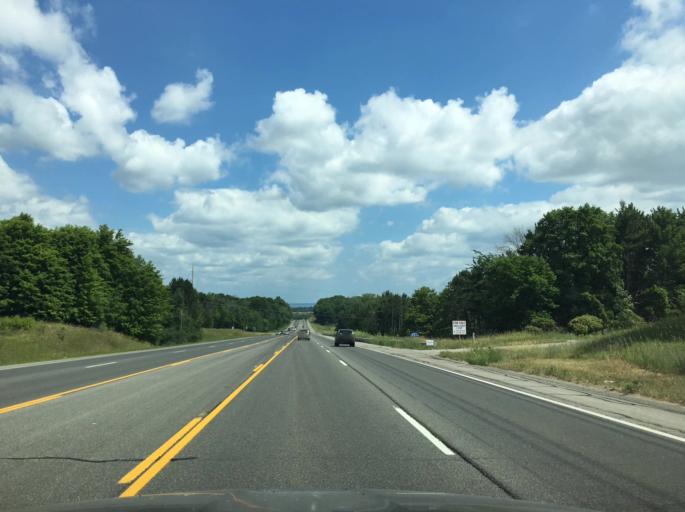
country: US
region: Michigan
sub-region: Grand Traverse County
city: Traverse City
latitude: 44.7053
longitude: -85.6535
